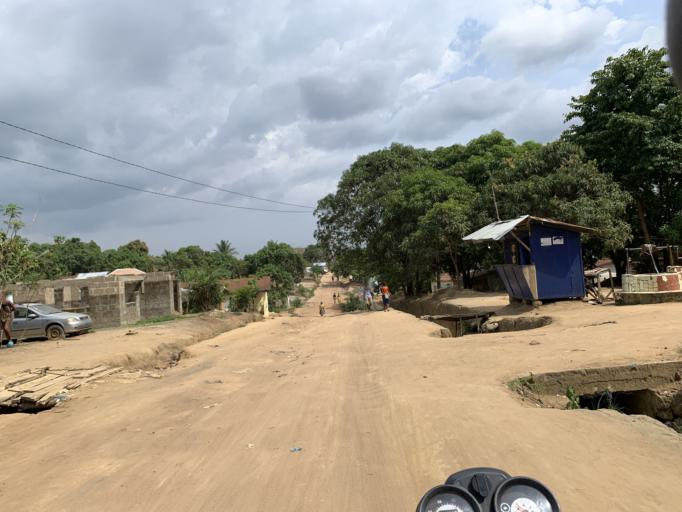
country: SL
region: Western Area
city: Waterloo
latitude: 8.3360
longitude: -13.0528
